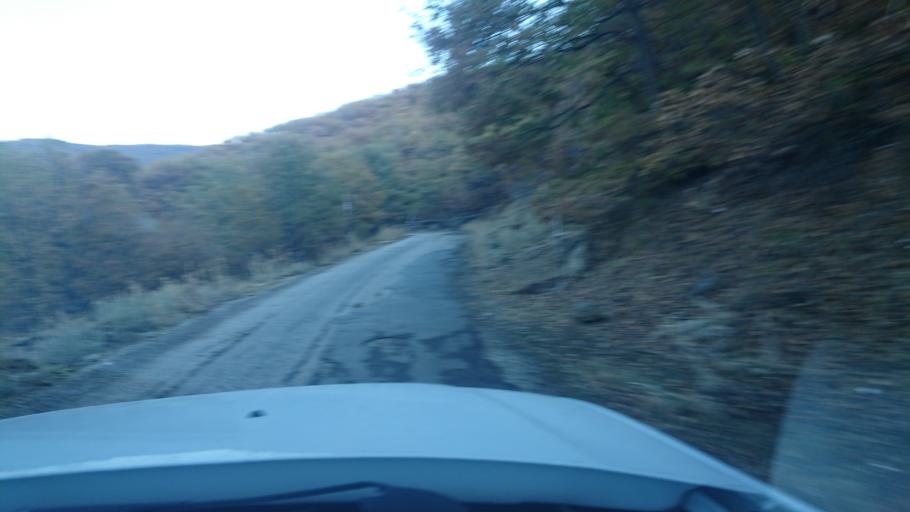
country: TR
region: Aksaray
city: Taspinar
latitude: 38.1656
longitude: 34.2000
